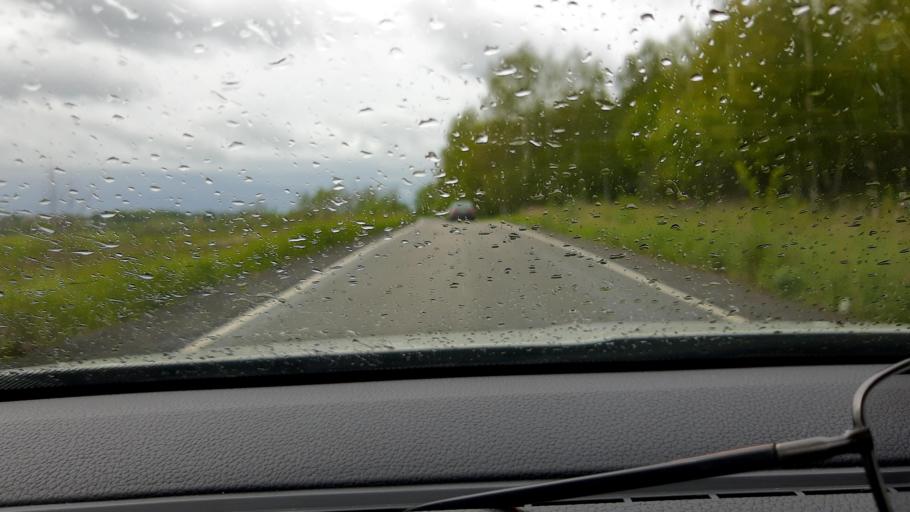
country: RU
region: Moskovskaya
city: Nikolina Gora
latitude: 55.7467
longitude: 36.9829
